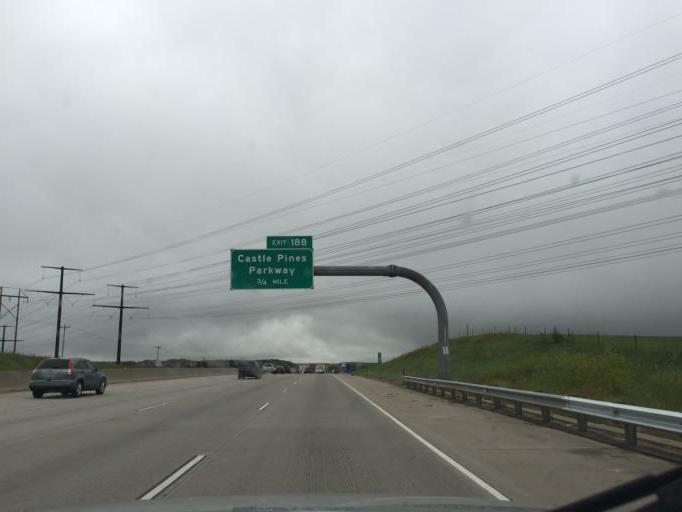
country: US
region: Colorado
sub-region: Douglas County
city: Castle Pines
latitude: 39.4572
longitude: -104.8749
